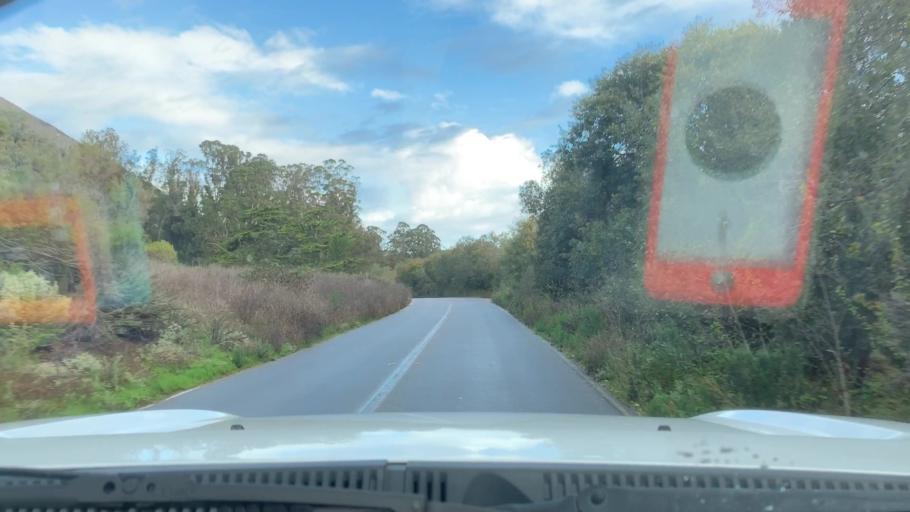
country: US
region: California
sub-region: San Luis Obispo County
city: Morro Bay
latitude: 35.3522
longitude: -120.8307
